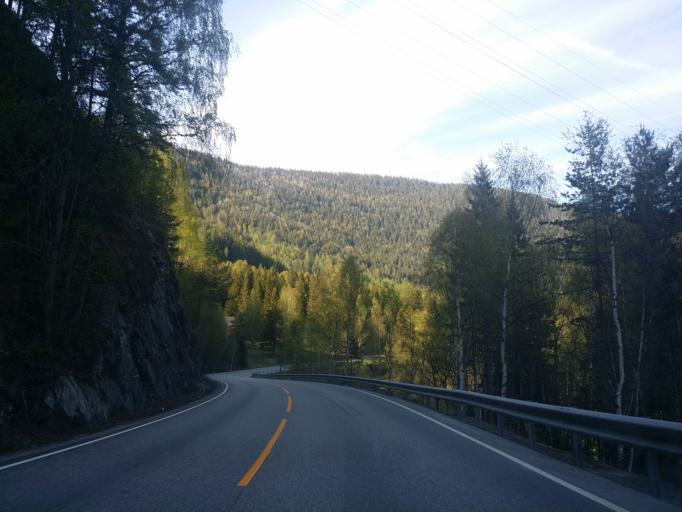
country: NO
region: Telemark
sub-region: Hjartdal
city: Sauland
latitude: 59.6141
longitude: 8.7893
